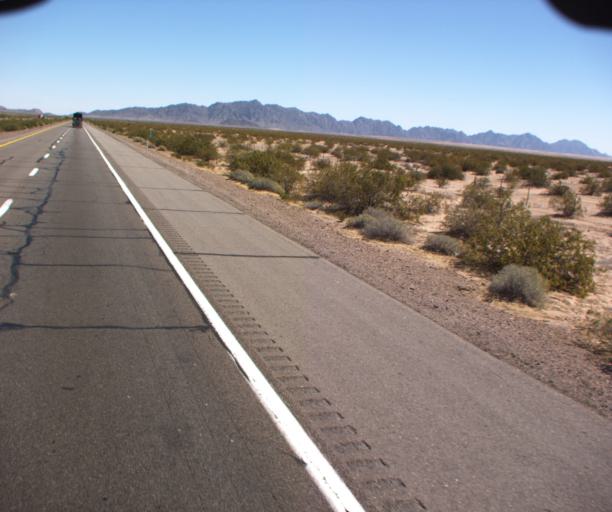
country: US
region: Arizona
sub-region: Yuma County
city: Wellton
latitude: 32.7085
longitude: -113.8537
